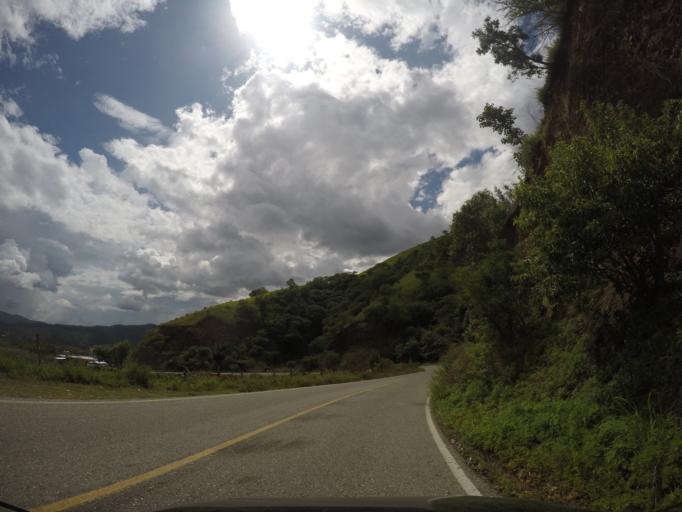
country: MX
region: Oaxaca
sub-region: San Jeronimo Coatlan
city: San Cristobal Honduras
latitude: 16.4336
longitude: -97.0581
